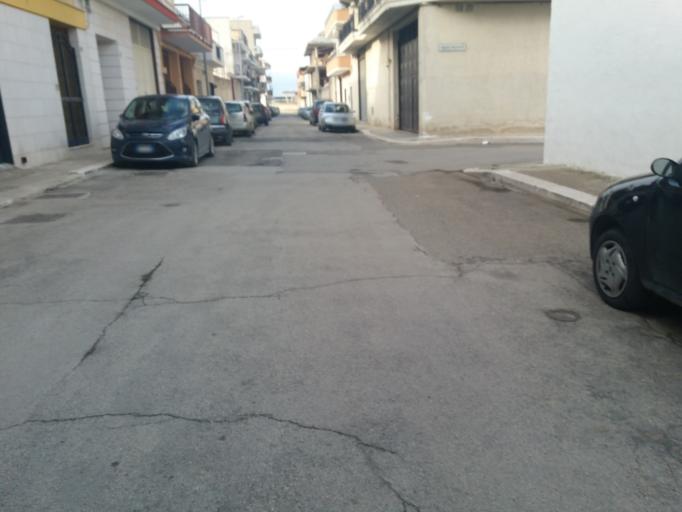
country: IT
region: Apulia
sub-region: Provincia di Barletta - Andria - Trani
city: Andria
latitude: 41.2405
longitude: 16.2898
